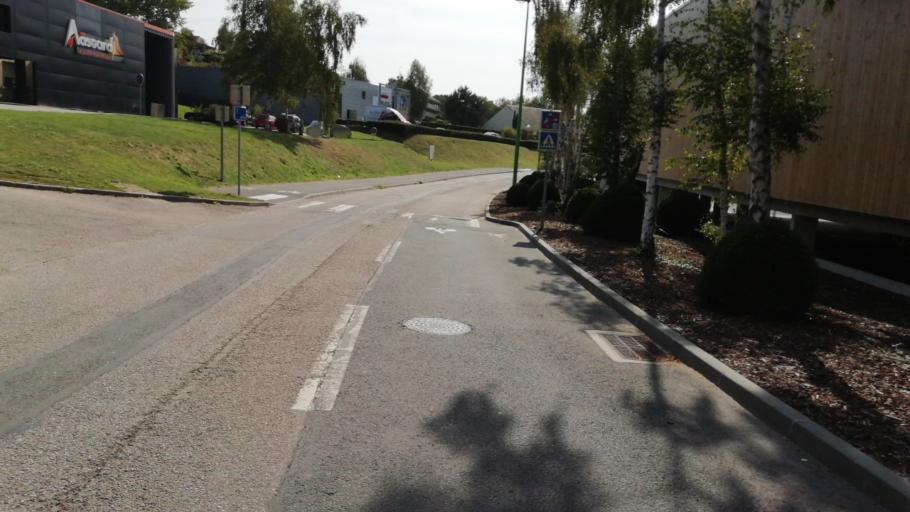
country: FR
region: Haute-Normandie
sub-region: Departement de la Seine-Maritime
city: Montivilliers
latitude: 49.5354
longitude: 0.1860
